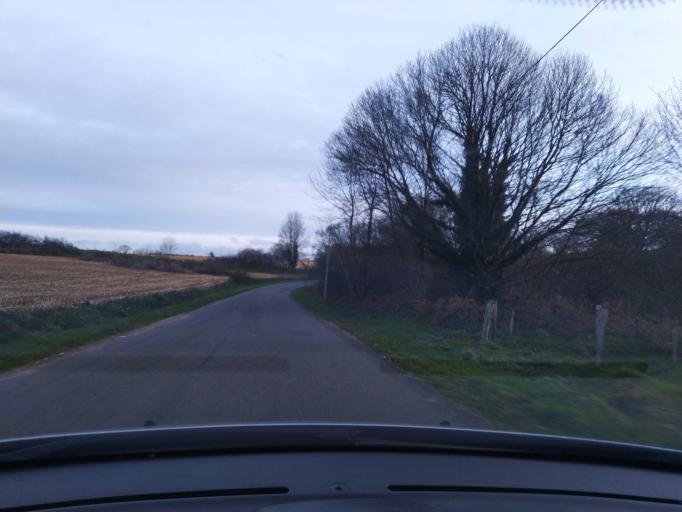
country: FR
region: Brittany
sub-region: Departement du Finistere
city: Guerlesquin
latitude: 48.5224
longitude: -3.5978
